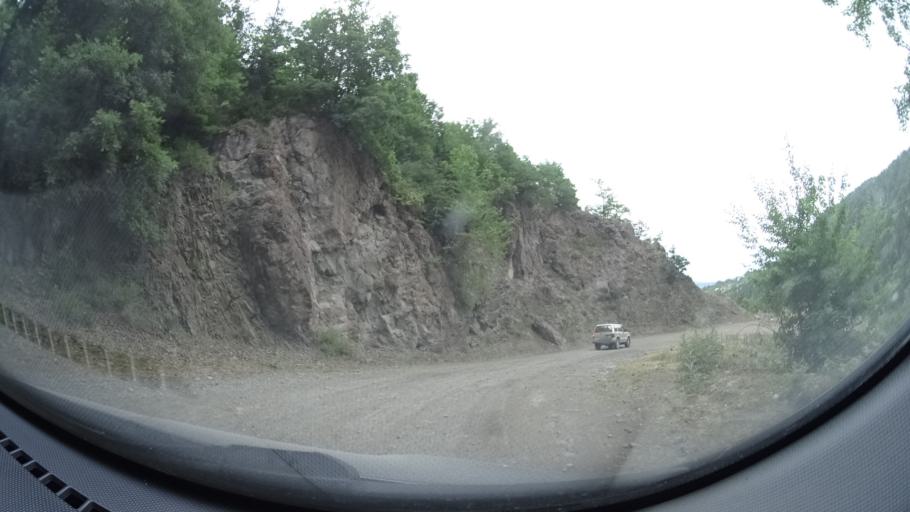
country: GE
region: Samtskhe-Javakheti
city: Adigeni
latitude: 41.6750
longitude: 42.6409
